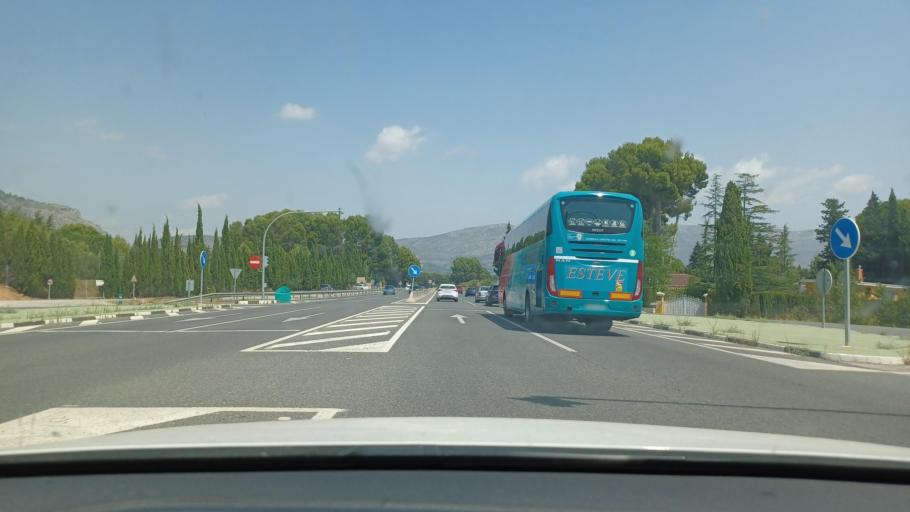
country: ES
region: Valencia
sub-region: Provincia de Alicante
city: Muro del Alcoy
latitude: 38.7658
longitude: -0.4444
